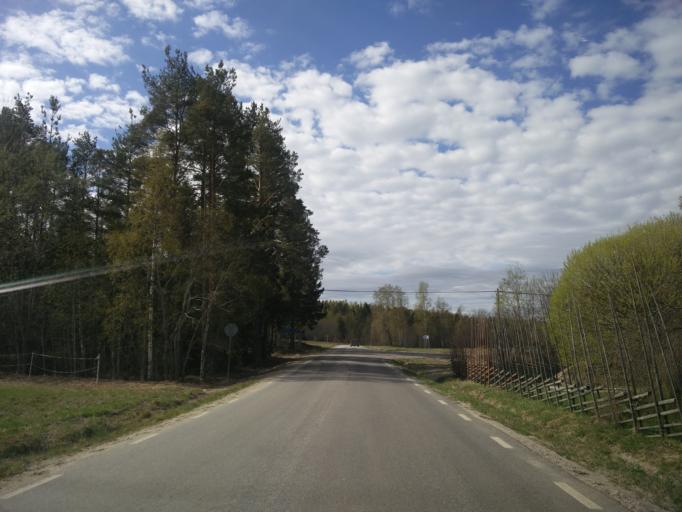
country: SE
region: Vaesternorrland
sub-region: Sundsvalls Kommun
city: Nolby
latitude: 62.2539
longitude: 17.3274
